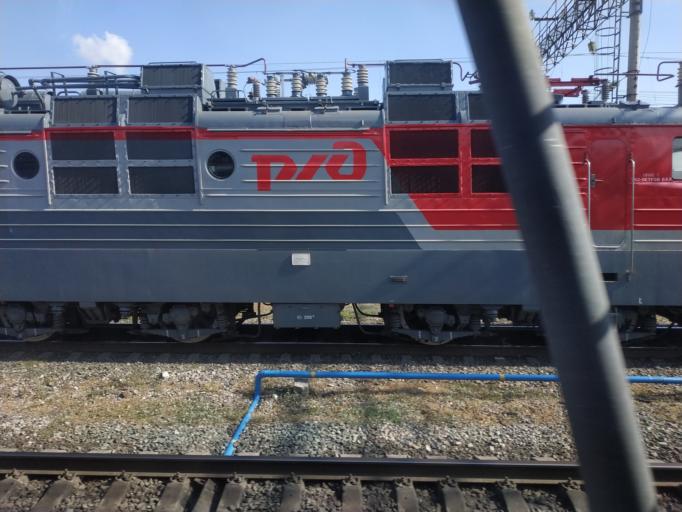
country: RU
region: Volgograd
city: Gumrak
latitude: 48.7781
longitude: 44.3792
